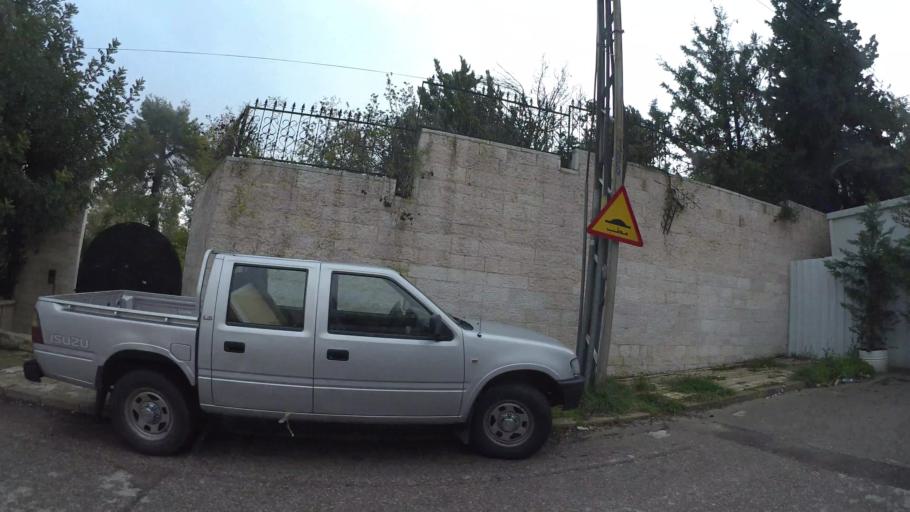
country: JO
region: Amman
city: Amman
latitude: 31.9614
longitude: 35.8829
